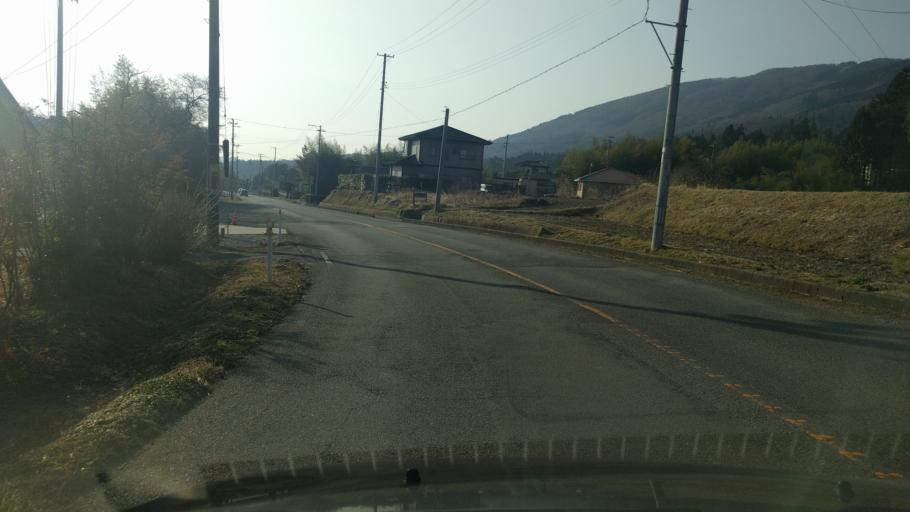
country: JP
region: Fukushima
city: Iwaki
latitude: 37.0509
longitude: 140.7952
